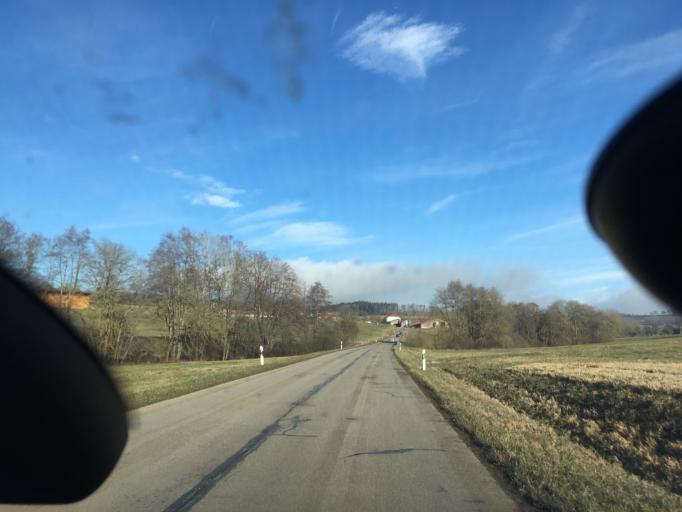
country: DE
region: Baden-Wuerttemberg
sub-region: Freiburg Region
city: Dogern
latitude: 47.6519
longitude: 8.1433
